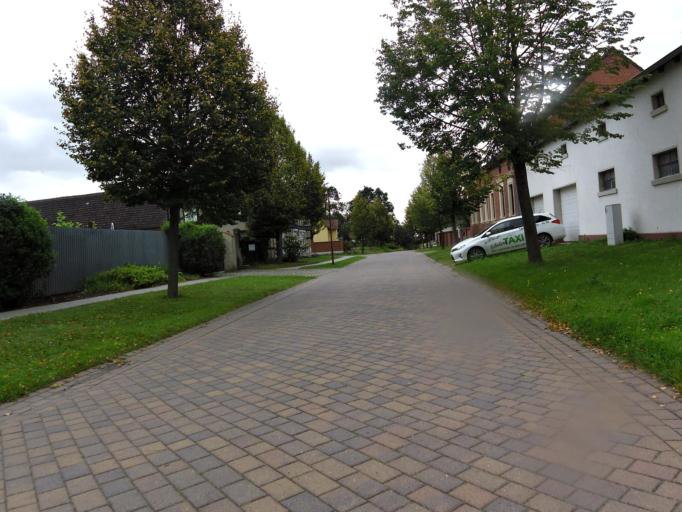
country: DE
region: Saxony-Anhalt
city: Tangermunde
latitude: 52.5894
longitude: 11.9872
